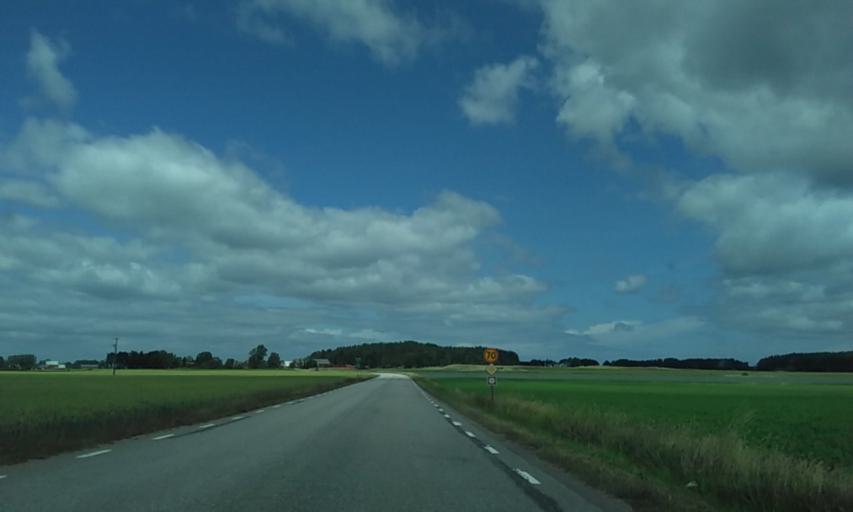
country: SE
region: Vaestra Goetaland
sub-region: Grastorps Kommun
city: Graestorp
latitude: 58.3561
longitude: 12.6787
